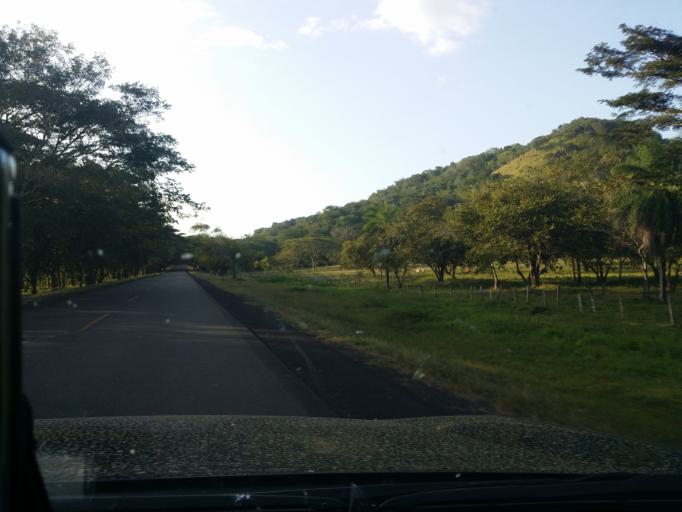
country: NI
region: Rio San Juan
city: San Miguelito
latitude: 11.3994
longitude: -84.8247
